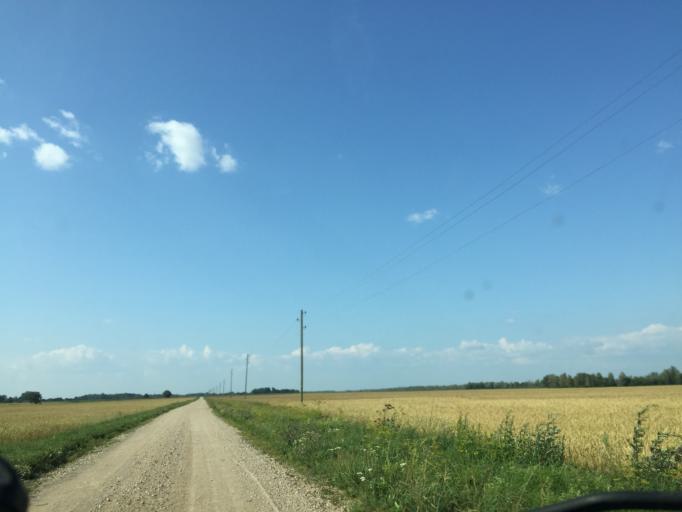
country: LV
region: Jelgava
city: Jelgava
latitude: 56.4579
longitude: 23.6808
